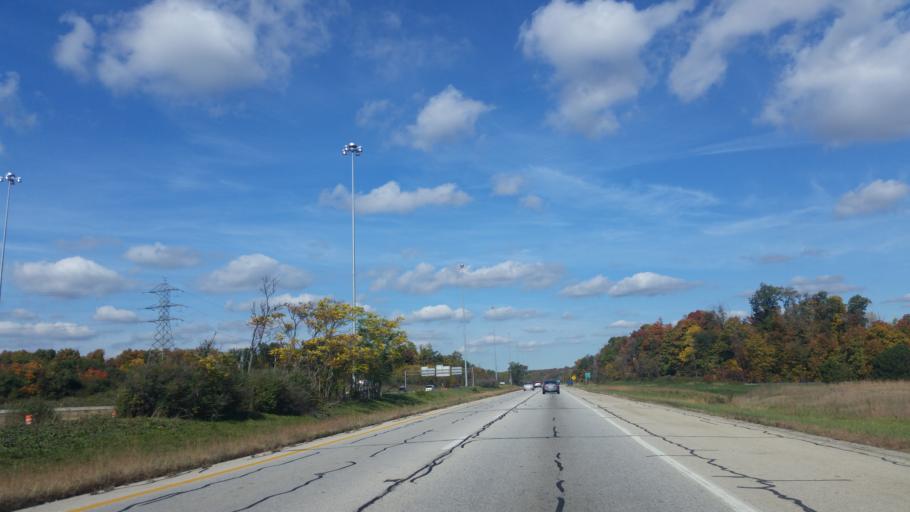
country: US
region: Ohio
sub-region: Summit County
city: Richfield
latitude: 41.2307
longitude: -81.6274
